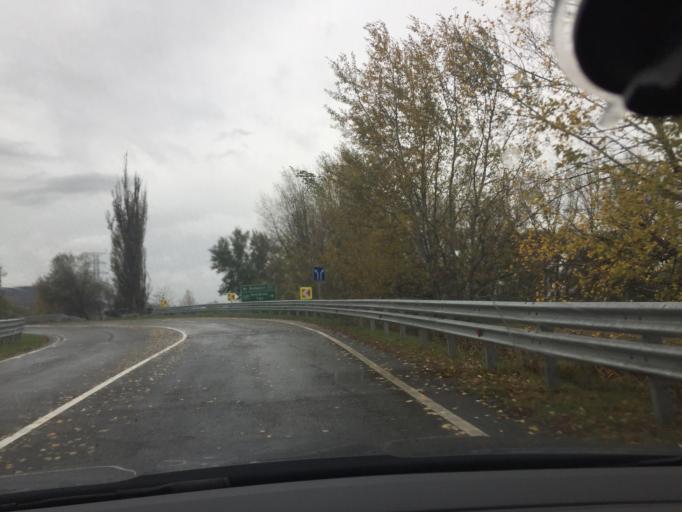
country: HU
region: Komarom-Esztergom
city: Tokod
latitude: 47.7516
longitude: 18.6929
